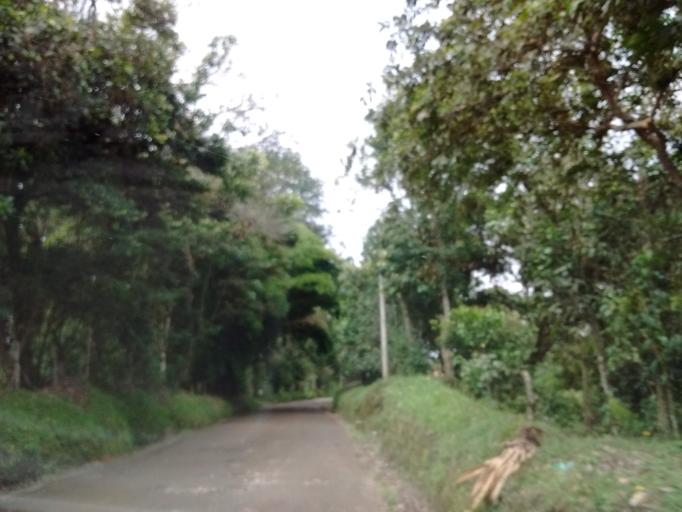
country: CO
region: Cauca
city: Popayan
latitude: 2.5288
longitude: -76.6068
